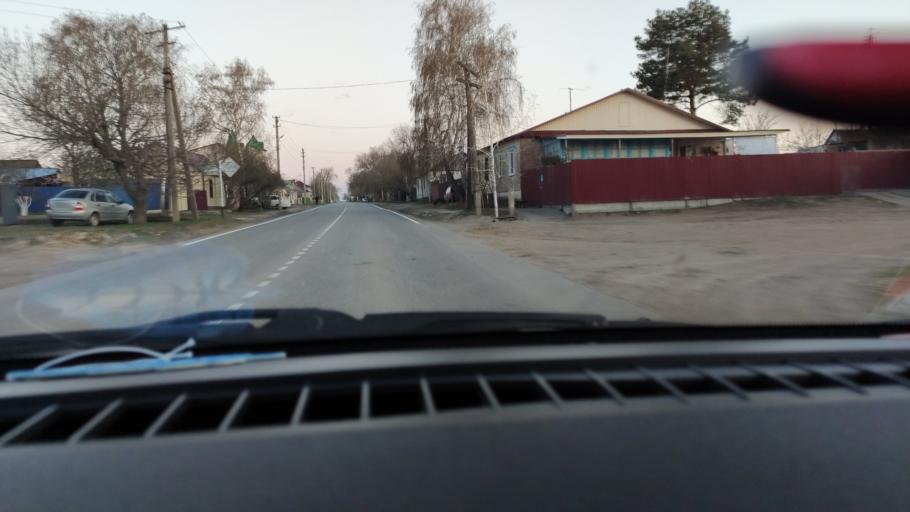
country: RU
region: Saratov
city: Privolzhskiy
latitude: 51.1861
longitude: 45.9173
